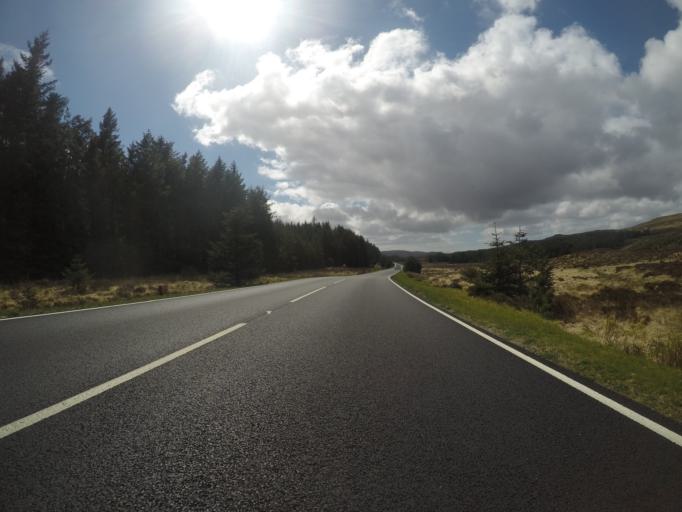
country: GB
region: Scotland
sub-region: Highland
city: Isle of Skye
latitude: 57.3336
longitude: -6.1989
